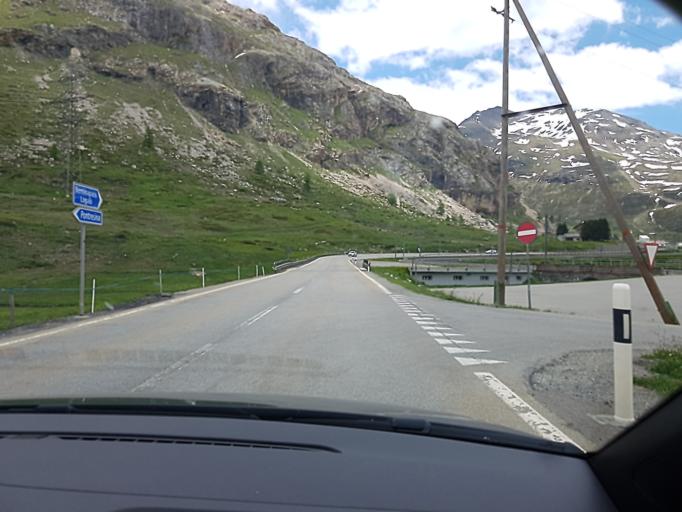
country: CH
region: Grisons
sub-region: Maloja District
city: Pontresina
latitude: 46.4422
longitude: 9.9833
